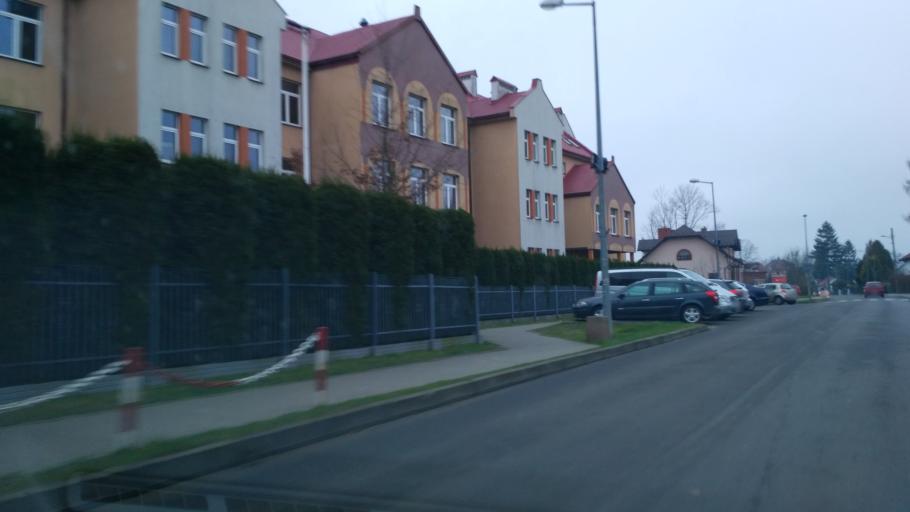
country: PL
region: Subcarpathian Voivodeship
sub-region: Powiat przeworski
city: Przeworsk
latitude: 50.0600
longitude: 22.5039
